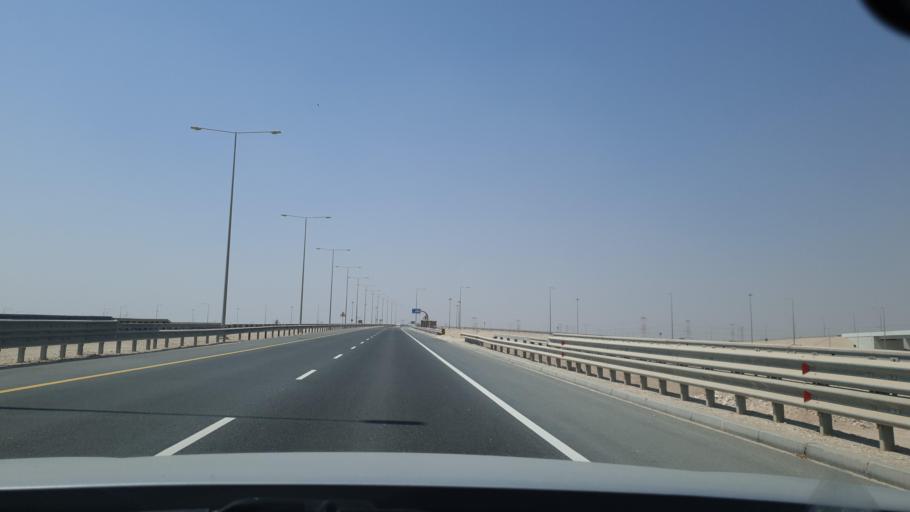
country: QA
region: Baladiyat az Za`ayin
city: Az Za`ayin
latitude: 25.6180
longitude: 51.3738
